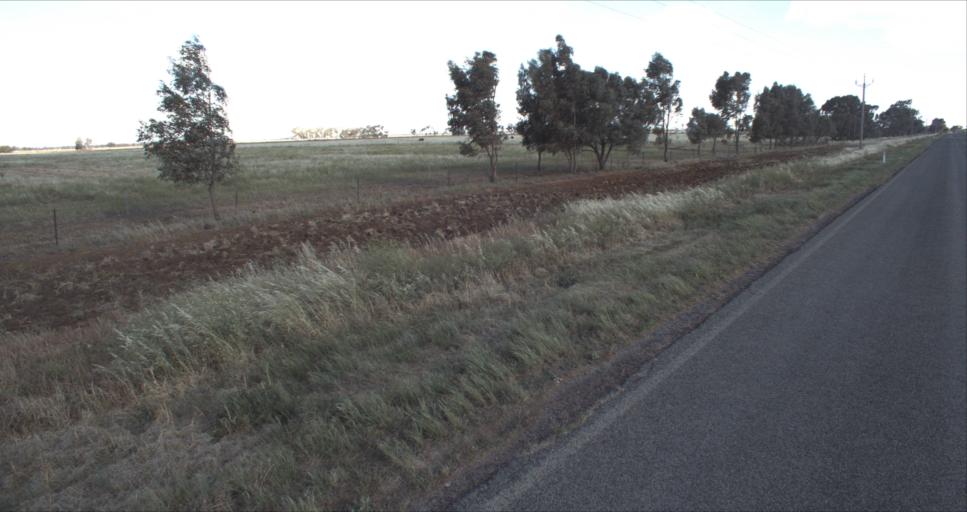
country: AU
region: New South Wales
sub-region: Leeton
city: Leeton
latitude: -34.5316
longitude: 146.2813
